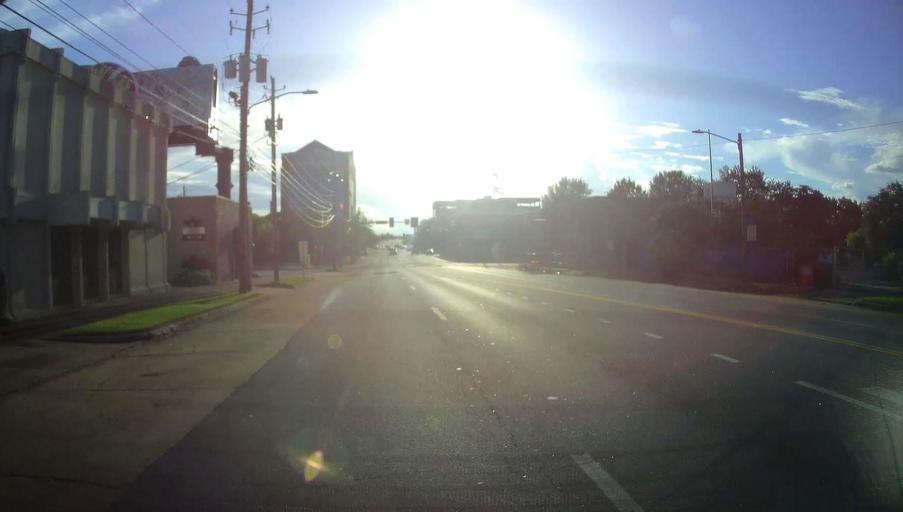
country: US
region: Georgia
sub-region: Muscogee County
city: Columbus
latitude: 32.4705
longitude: -84.9894
